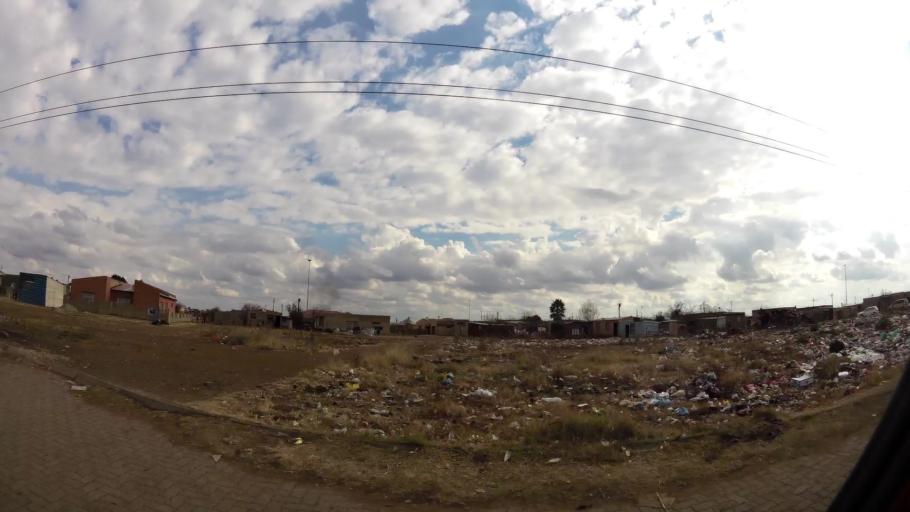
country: ZA
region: Gauteng
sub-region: Sedibeng District Municipality
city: Vanderbijlpark
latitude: -26.6977
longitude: 27.7909
